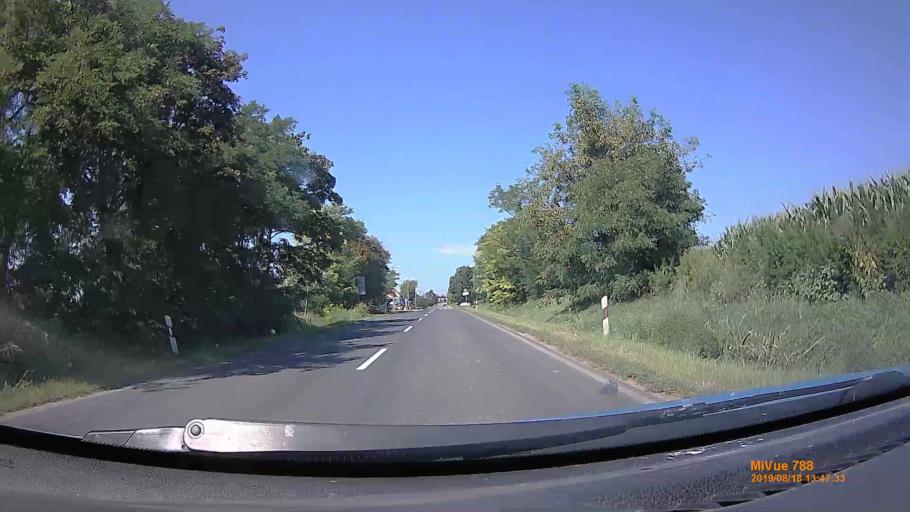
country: HU
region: Fejer
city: Cece
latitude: 46.7538
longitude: 18.6407
